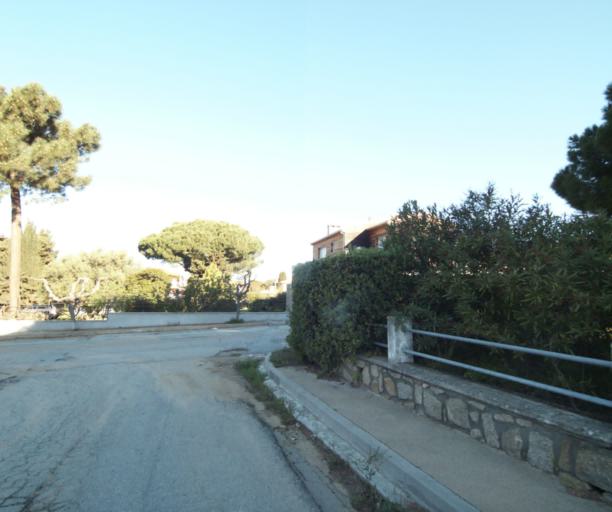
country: FR
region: Corsica
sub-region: Departement de la Corse-du-Sud
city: Propriano
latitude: 41.6709
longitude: 8.9141
